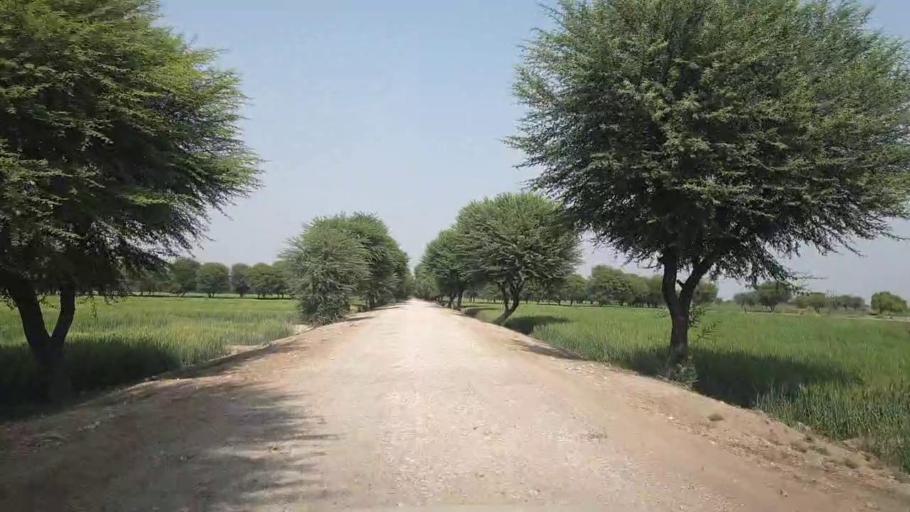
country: PK
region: Sindh
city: Dhoro Naro
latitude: 25.4797
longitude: 69.6203
